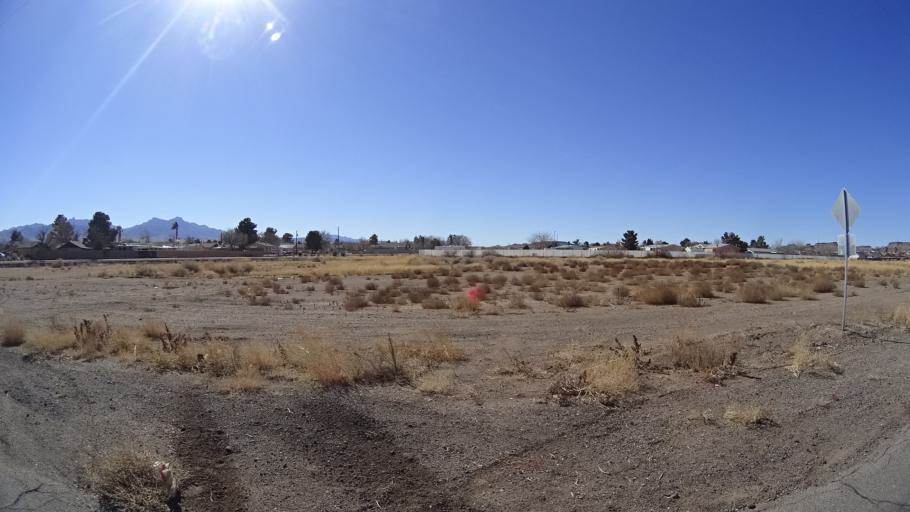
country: US
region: Arizona
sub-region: Mohave County
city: New Kingman-Butler
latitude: 35.2326
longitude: -114.0300
